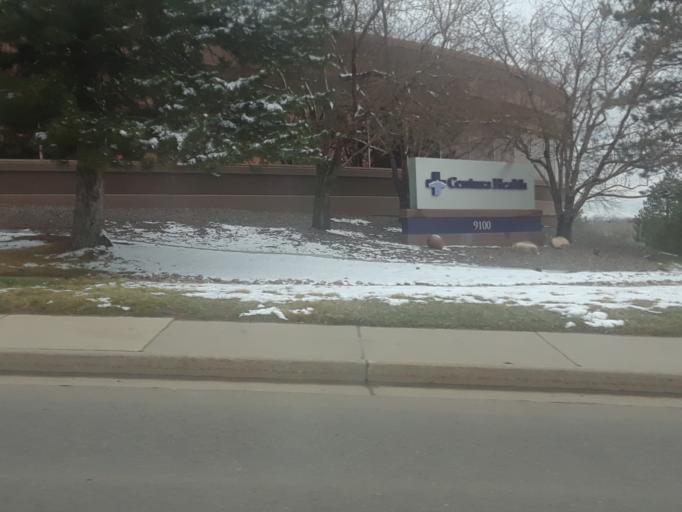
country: US
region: Colorado
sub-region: Arapahoe County
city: Centennial
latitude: 39.5758
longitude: -104.8818
